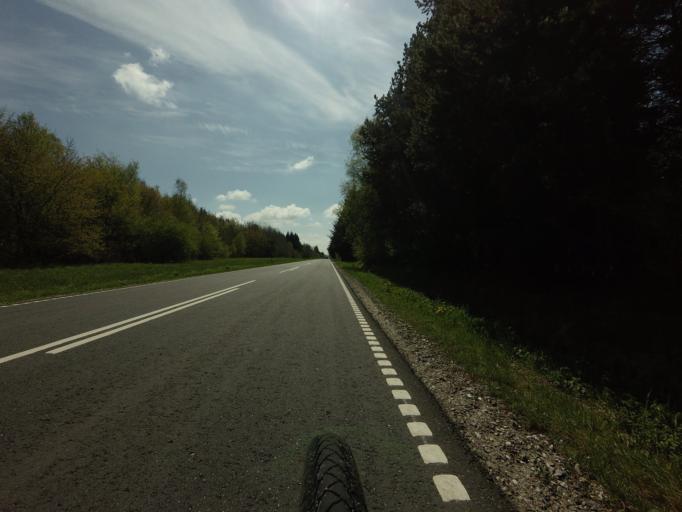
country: DK
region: North Denmark
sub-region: Jammerbugt Kommune
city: Brovst
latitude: 57.1615
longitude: 9.5754
